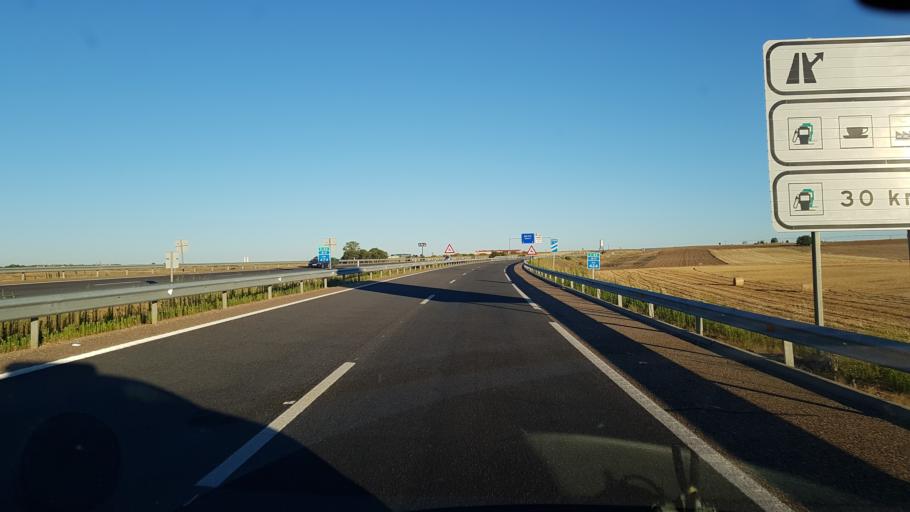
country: ES
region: Castille and Leon
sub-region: Provincia de Zamora
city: Toro
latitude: 41.5396
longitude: -5.3656
